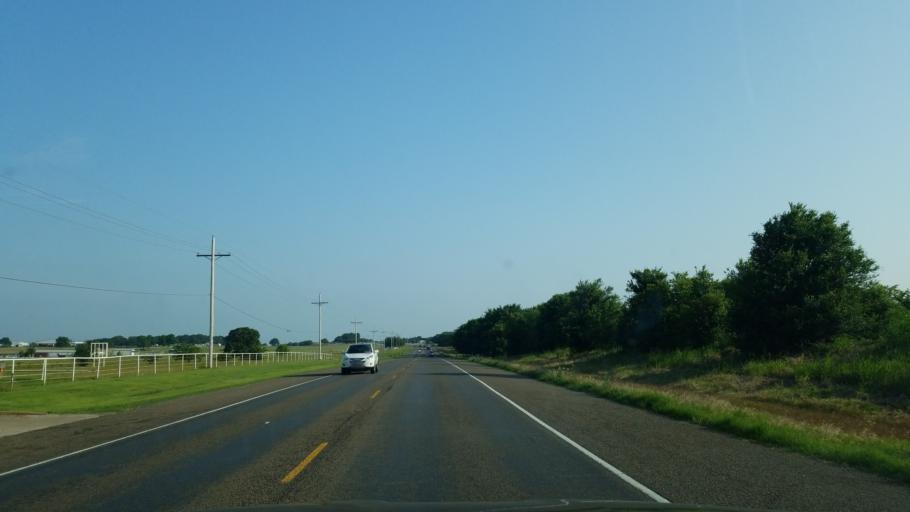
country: US
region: Texas
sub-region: Denton County
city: Aubrey
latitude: 33.3388
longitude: -96.9696
